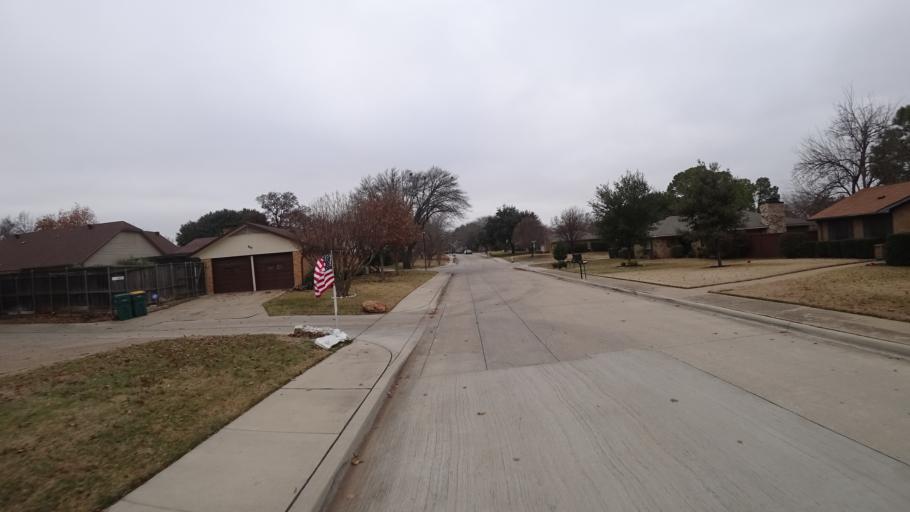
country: US
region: Texas
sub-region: Denton County
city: Highland Village
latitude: 33.0513
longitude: -97.0392
